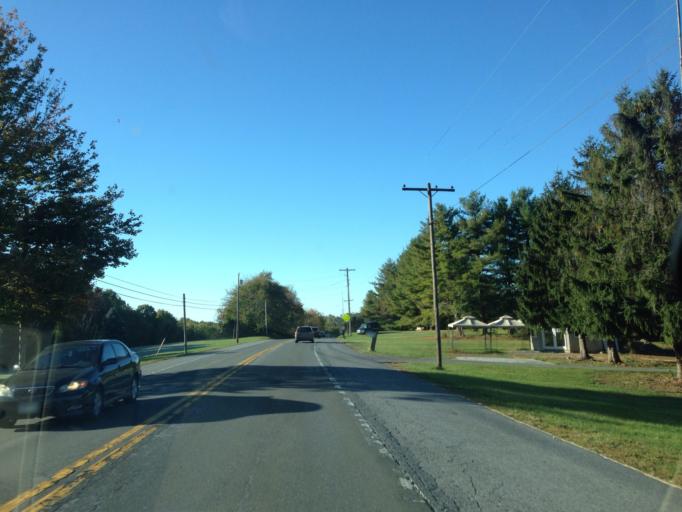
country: US
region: Maryland
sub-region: Carroll County
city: Mount Airy
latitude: 39.3416
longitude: -77.1829
